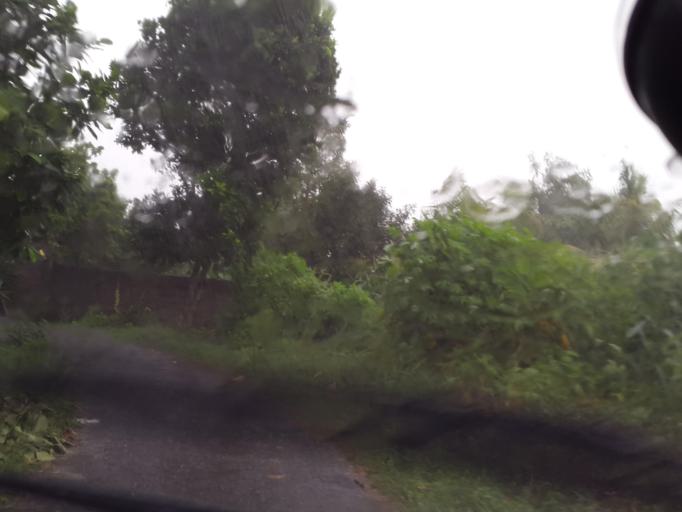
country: ID
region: West Nusa Tenggara
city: Karangkebon Timur
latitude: -8.6335
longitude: 116.1127
